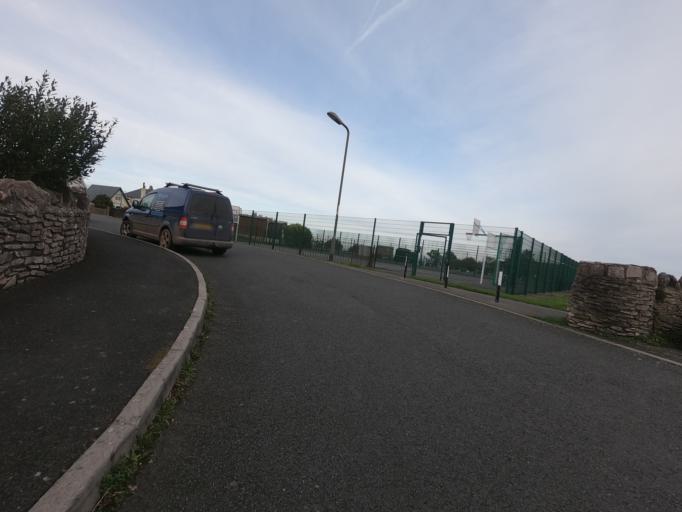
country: GB
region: England
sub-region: Borough of Torbay
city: Brixham
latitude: 50.3962
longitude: -3.5187
